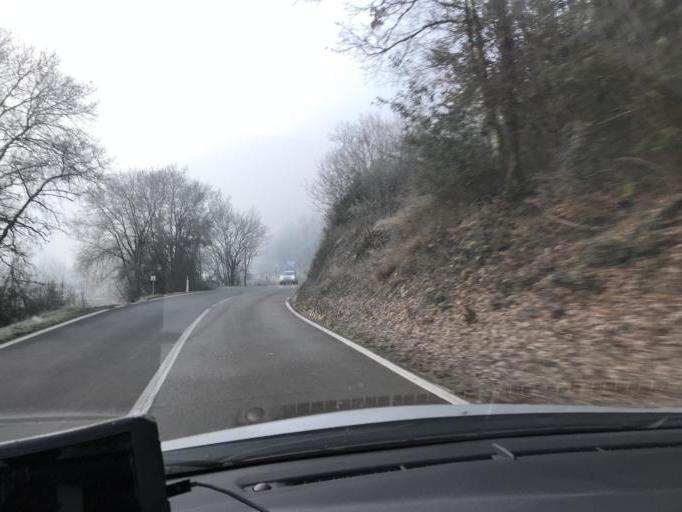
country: IT
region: Latium
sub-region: Provincia di Rieti
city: Colli sul Velino
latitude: 42.5098
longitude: 12.7395
